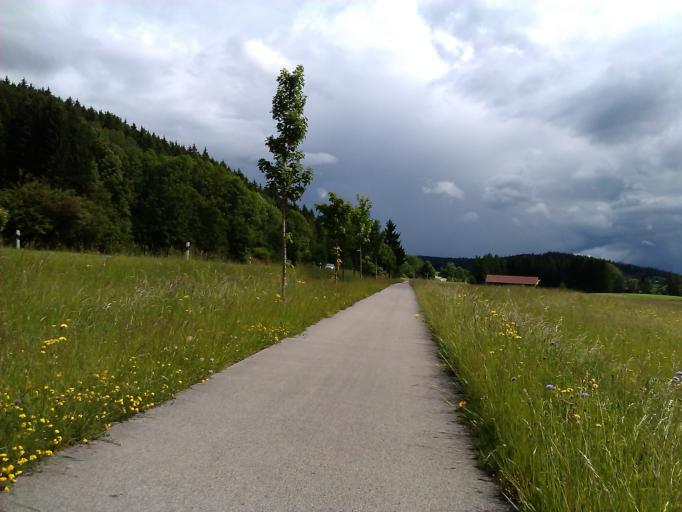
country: DE
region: Bavaria
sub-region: Swabia
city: Stotten am Auerberg
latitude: 47.7275
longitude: 10.6816
